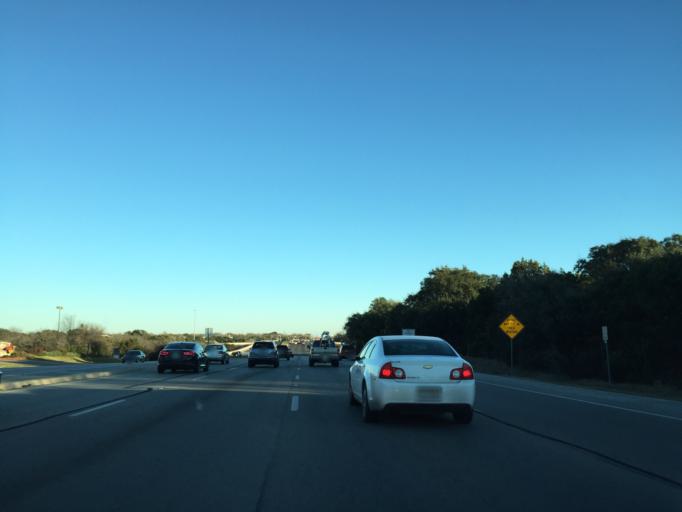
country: US
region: Texas
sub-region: Travis County
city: Wells Branch
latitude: 30.4236
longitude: -97.7107
